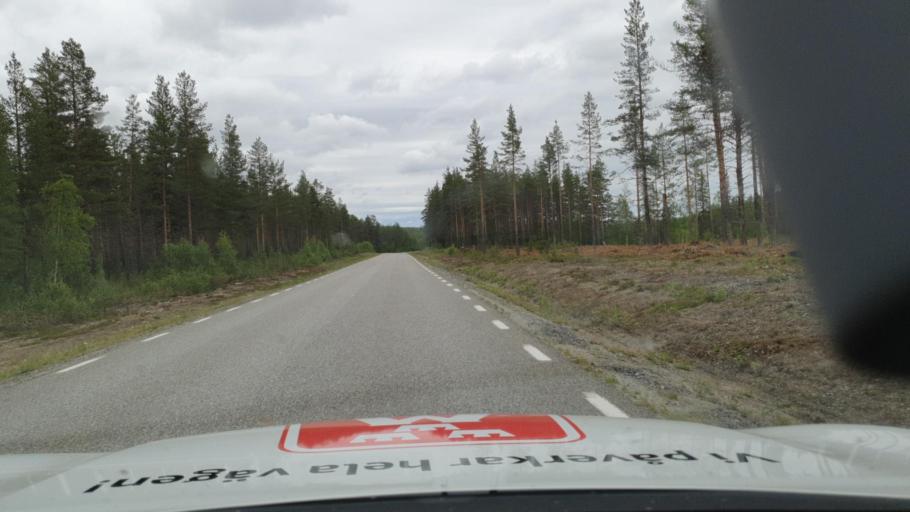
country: SE
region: Vaesterbotten
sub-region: Lycksele Kommun
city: Lycksele
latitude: 64.2042
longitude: 18.2903
